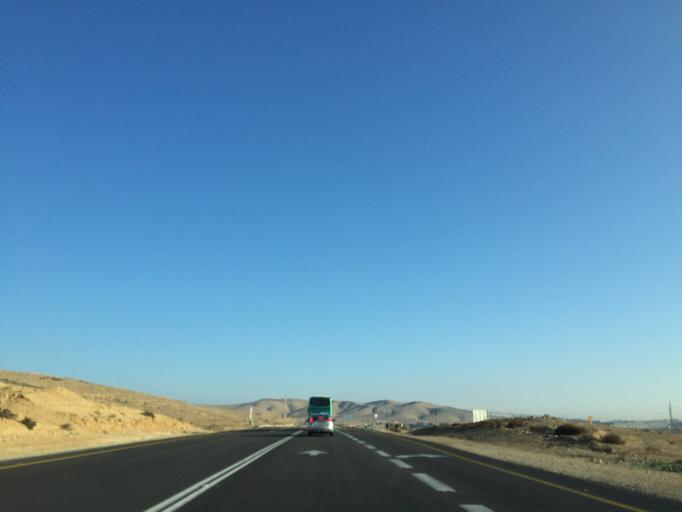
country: IL
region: Southern District
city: Dimona
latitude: 31.0551
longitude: 34.9980
